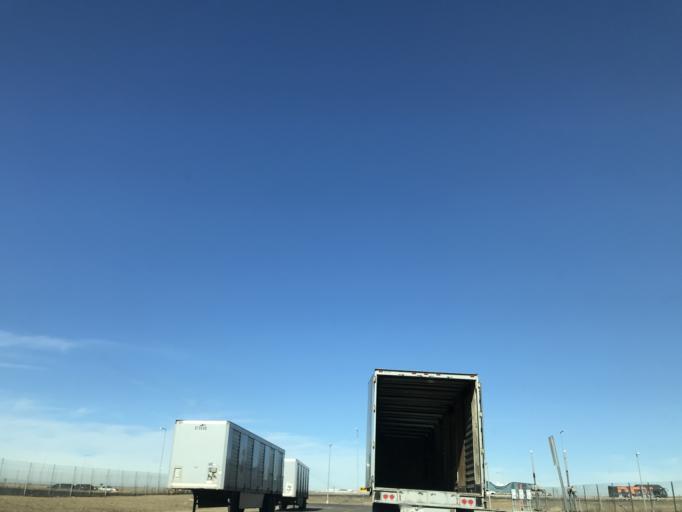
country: US
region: Colorado
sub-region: Weld County
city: Lochbuie
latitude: 39.8321
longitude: -104.6777
